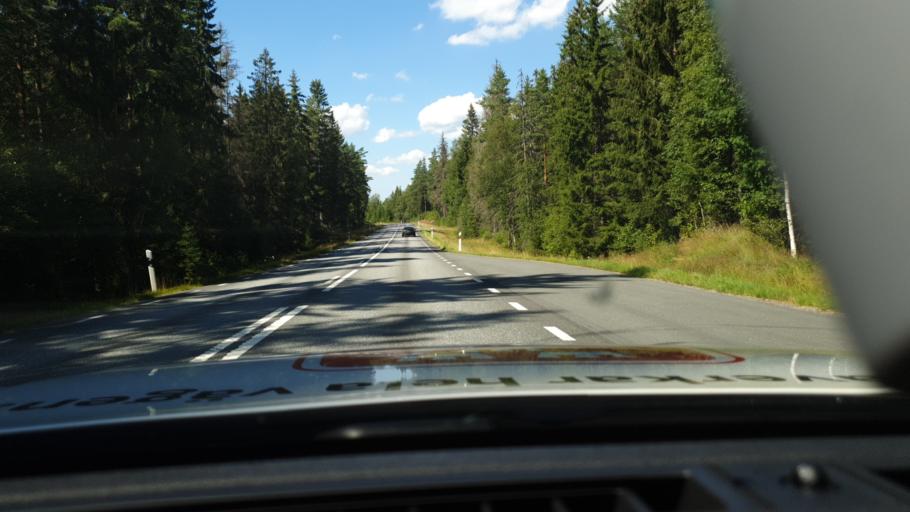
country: SE
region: Joenkoeping
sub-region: Savsjo Kommun
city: Vrigstad
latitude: 57.3956
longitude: 14.3784
